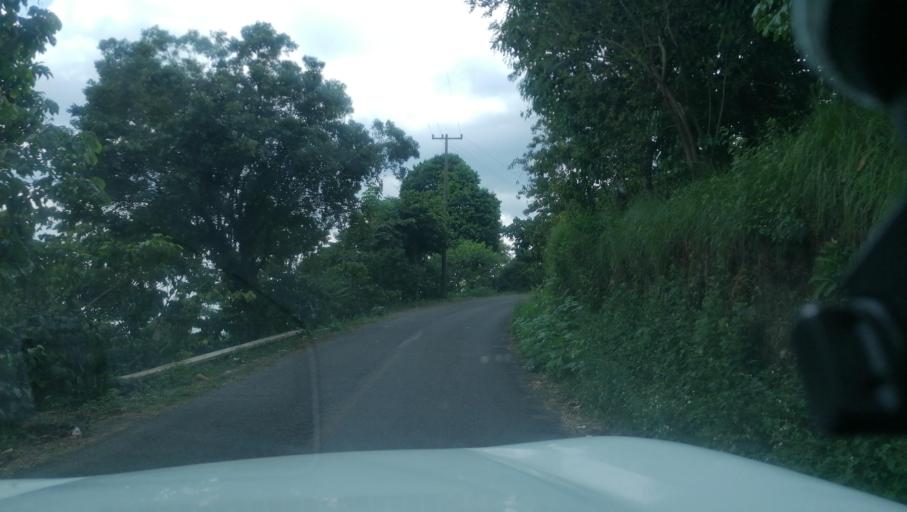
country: MX
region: Chiapas
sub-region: Cacahoatan
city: Benito Juarez
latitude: 15.0607
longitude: -92.1505
